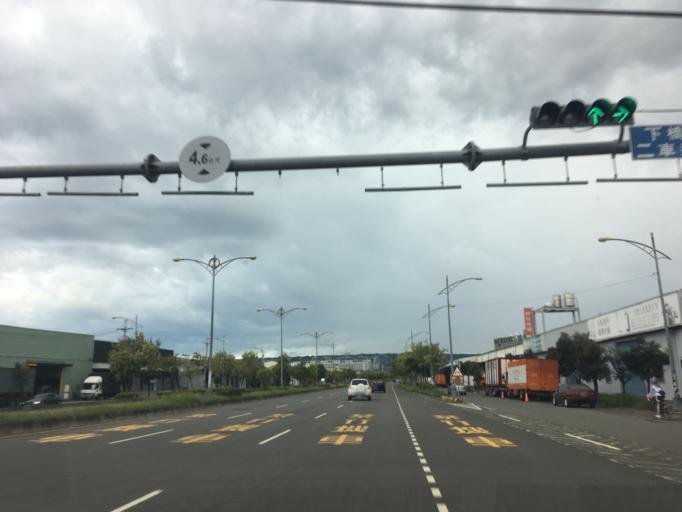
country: TW
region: Taiwan
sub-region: Taichung City
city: Taichung
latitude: 24.2017
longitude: 120.6438
